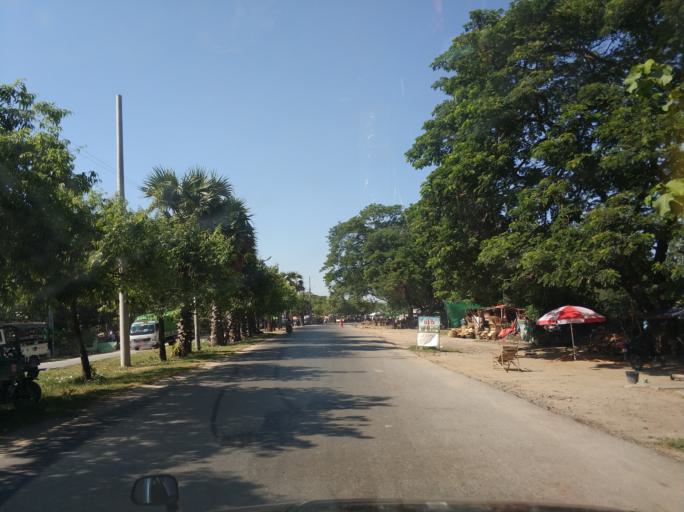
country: MM
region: Mandalay
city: Mandalay
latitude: 21.9630
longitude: 96.0559
